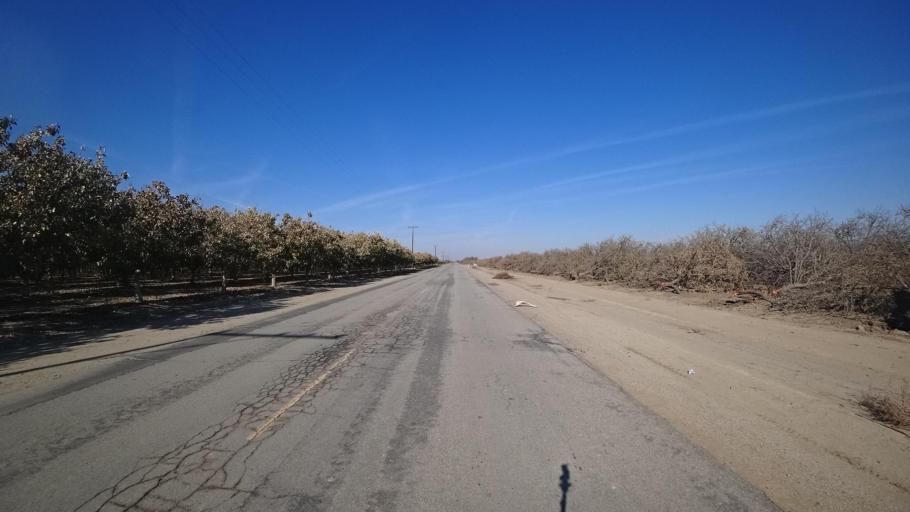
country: US
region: California
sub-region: Kern County
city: Wasco
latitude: 35.6614
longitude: -119.3486
